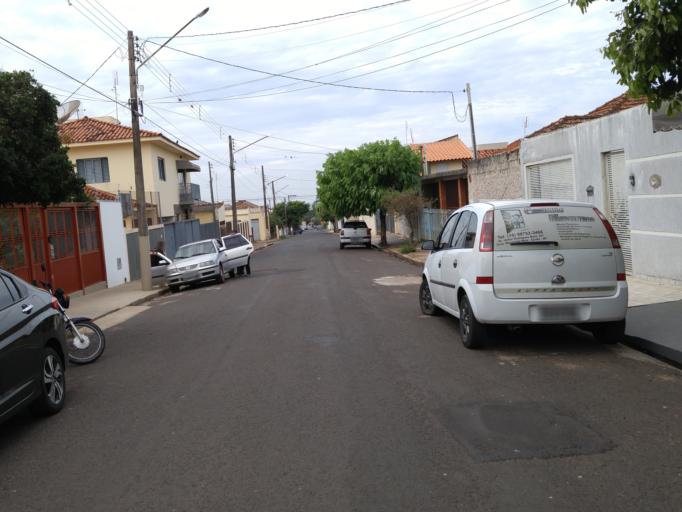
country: BR
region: Sao Paulo
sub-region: Paraguacu Paulista
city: Paraguacu Paulista
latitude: -22.4169
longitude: -50.5778
